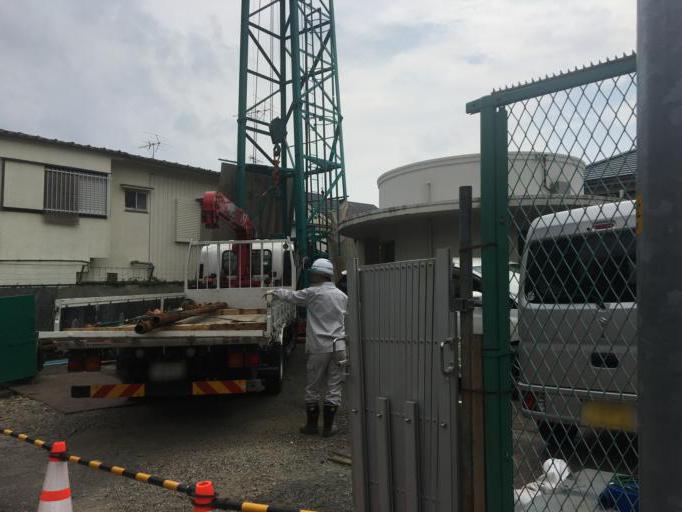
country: JP
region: Saitama
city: Yono
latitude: 35.8599
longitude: 139.6413
